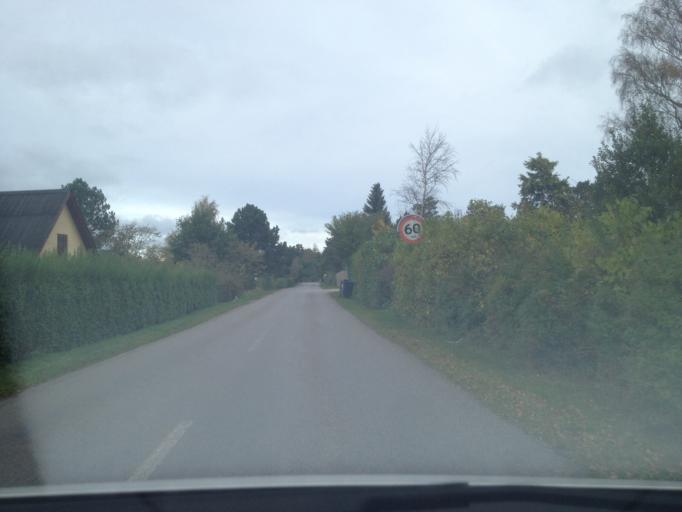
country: DK
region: Zealand
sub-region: Odsherred Kommune
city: Hojby
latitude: 55.9397
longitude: 11.6113
